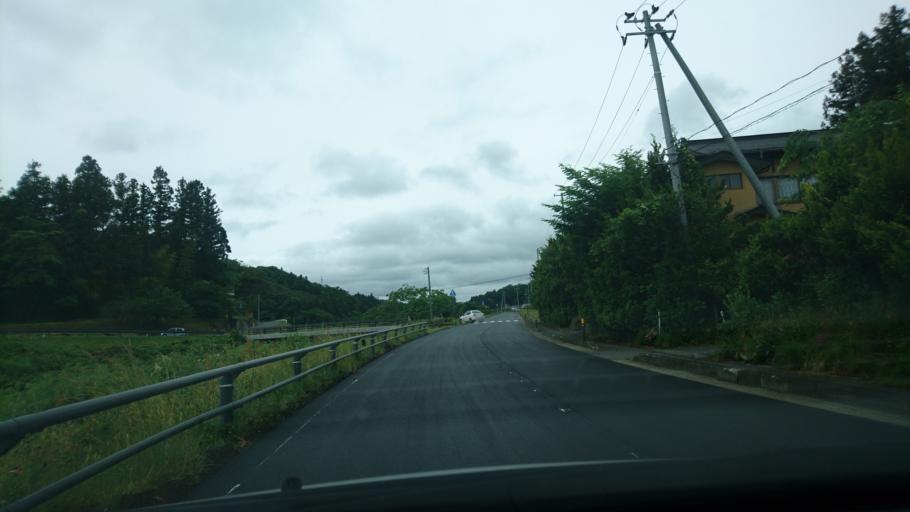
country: JP
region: Iwate
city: Ichinoseki
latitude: 38.9737
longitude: 141.0847
